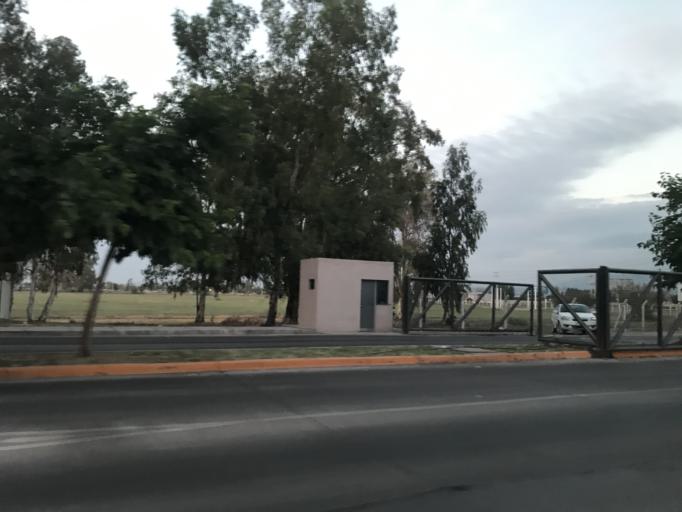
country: AR
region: Mendoza
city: Las Heras
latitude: -32.8277
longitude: -68.8033
